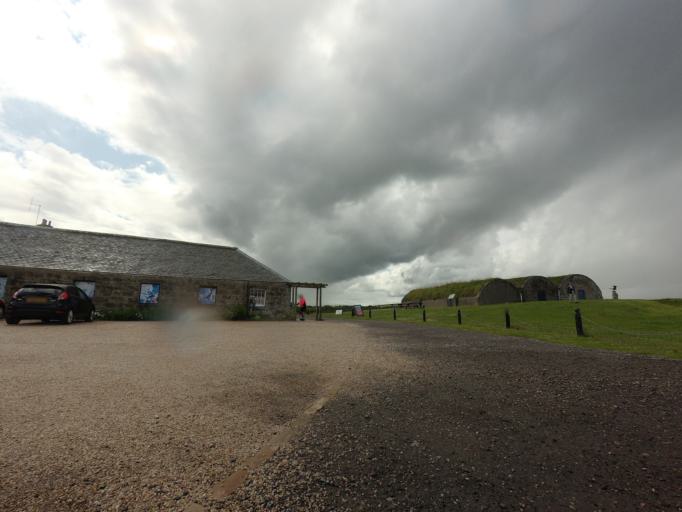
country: GB
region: Scotland
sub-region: Moray
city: Fochabers
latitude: 57.6737
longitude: -3.0929
